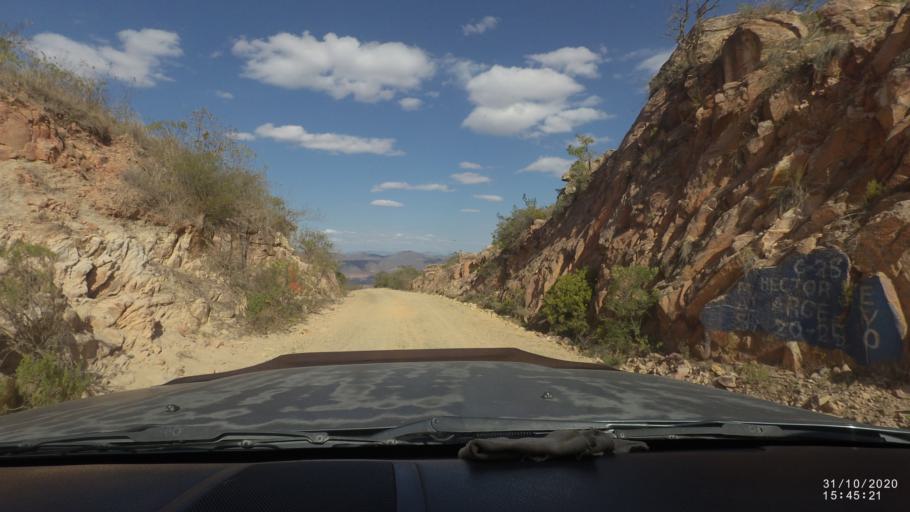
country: BO
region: Chuquisaca
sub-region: Provincia Zudanez
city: Mojocoya
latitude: -18.3192
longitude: -64.7171
